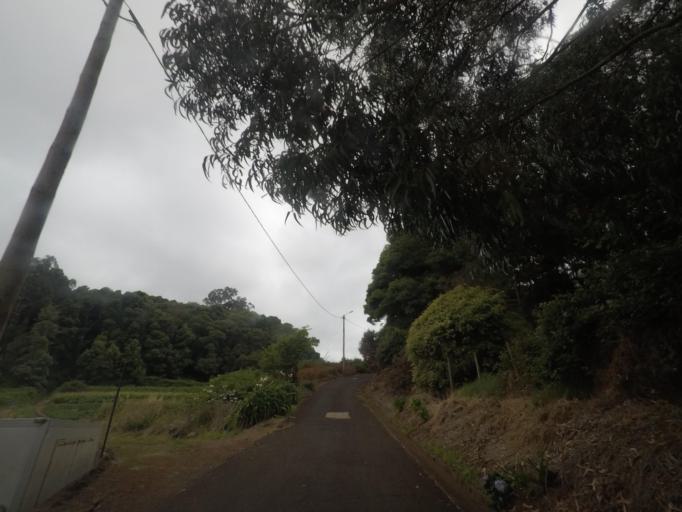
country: PT
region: Madeira
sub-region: Porto Moniz
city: Porto Moniz
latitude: 32.8620
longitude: -17.1837
